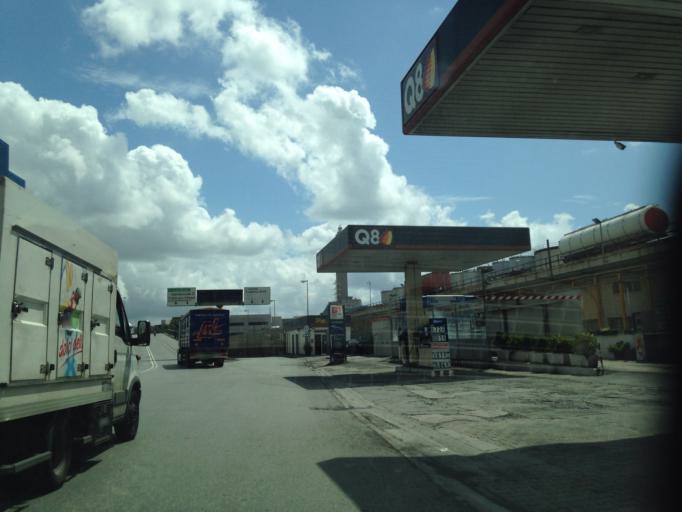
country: IT
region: Liguria
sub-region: Provincia di Genova
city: San Teodoro
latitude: 44.4072
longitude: 8.8979
